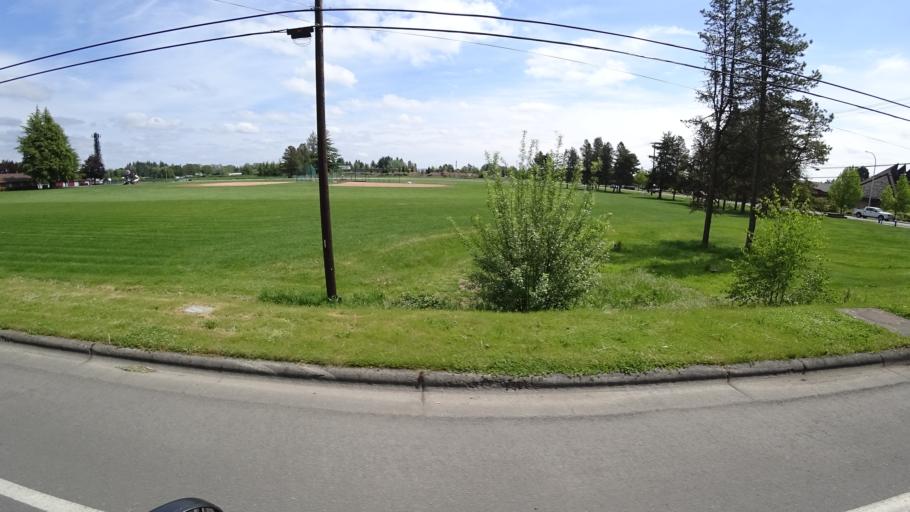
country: US
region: Oregon
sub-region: Washington County
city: Hillsboro
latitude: 45.5503
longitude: -122.9955
